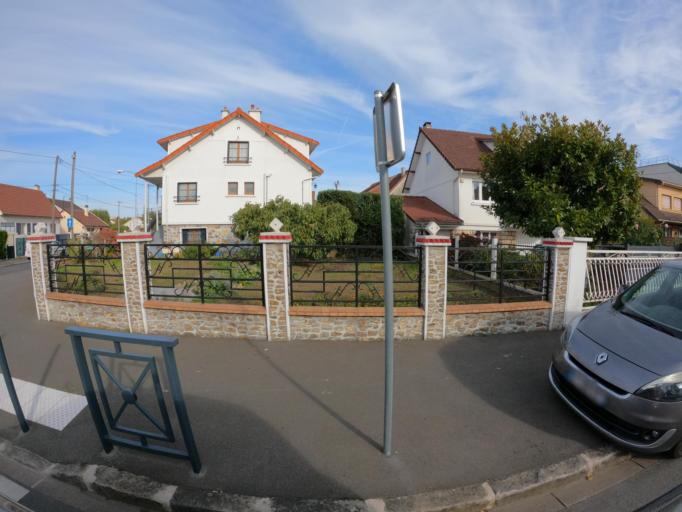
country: FR
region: Ile-de-France
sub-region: Departement de Seine-et-Marne
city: Pontault-Combault
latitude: 48.7950
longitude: 2.6076
